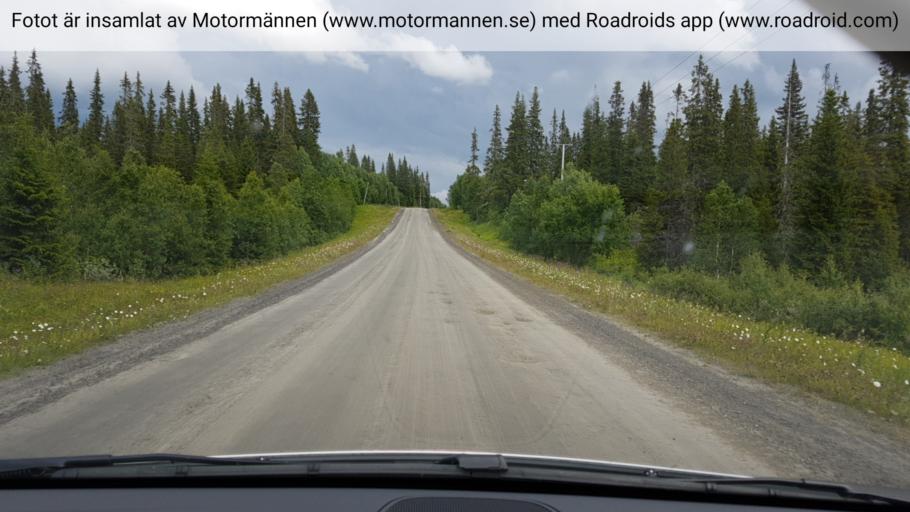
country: SE
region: Jaemtland
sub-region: Are Kommun
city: Are
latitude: 63.7029
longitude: 12.6942
